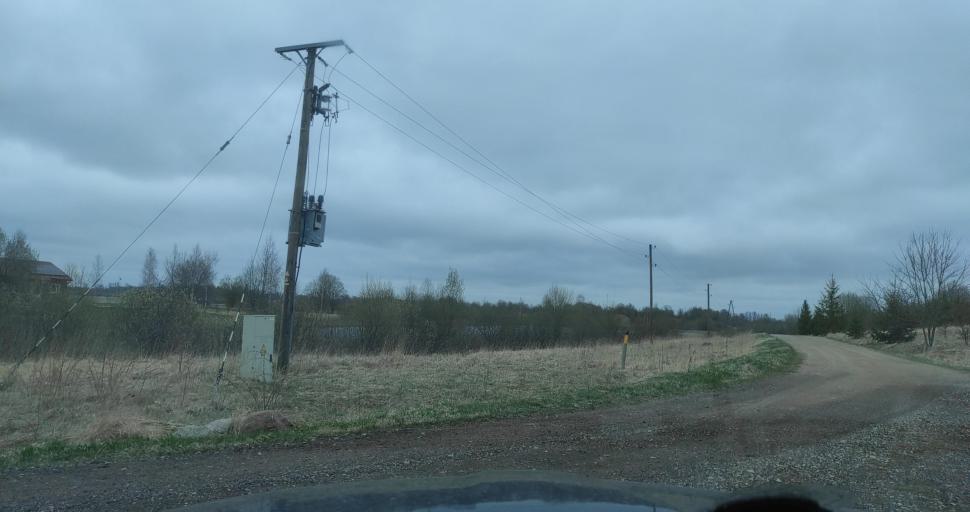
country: LV
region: Saldus Rajons
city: Saldus
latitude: 56.6354
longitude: 22.4196
